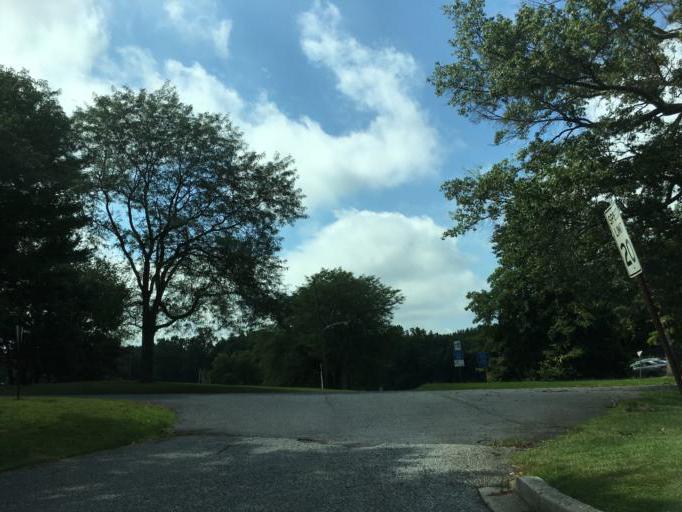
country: US
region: Maryland
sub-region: Anne Arundel County
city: Crownsville
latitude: 39.0262
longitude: -76.6041
